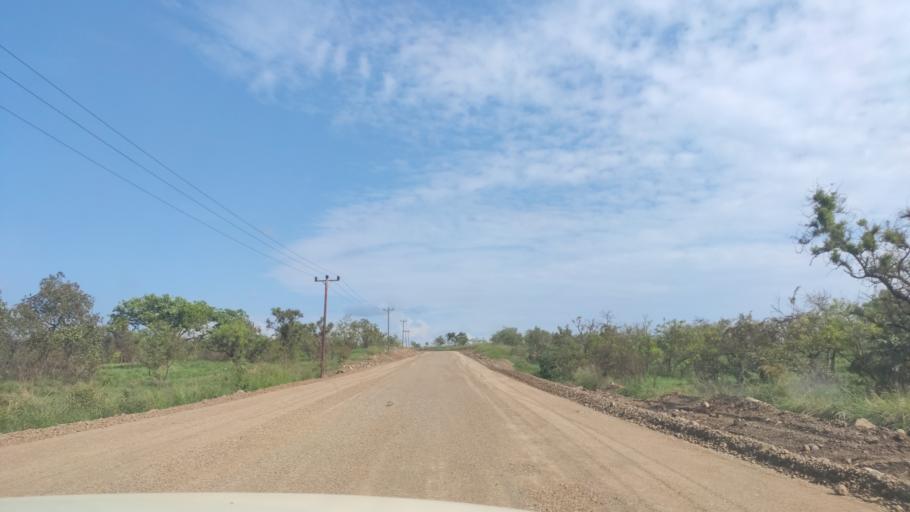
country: ET
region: Southern Nations, Nationalities, and People's Region
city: Felege Neway
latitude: 6.4258
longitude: 37.2182
